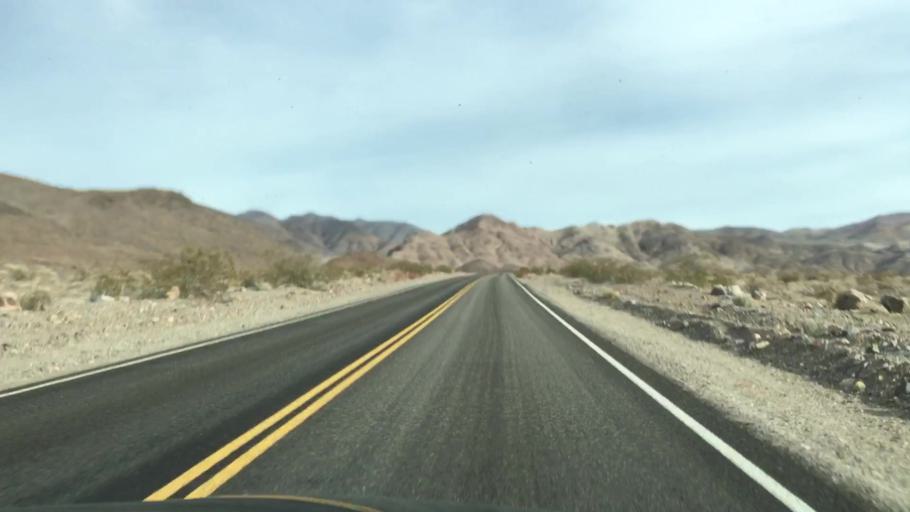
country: US
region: Nevada
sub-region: Nye County
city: Beatty
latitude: 36.7137
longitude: -116.9832
